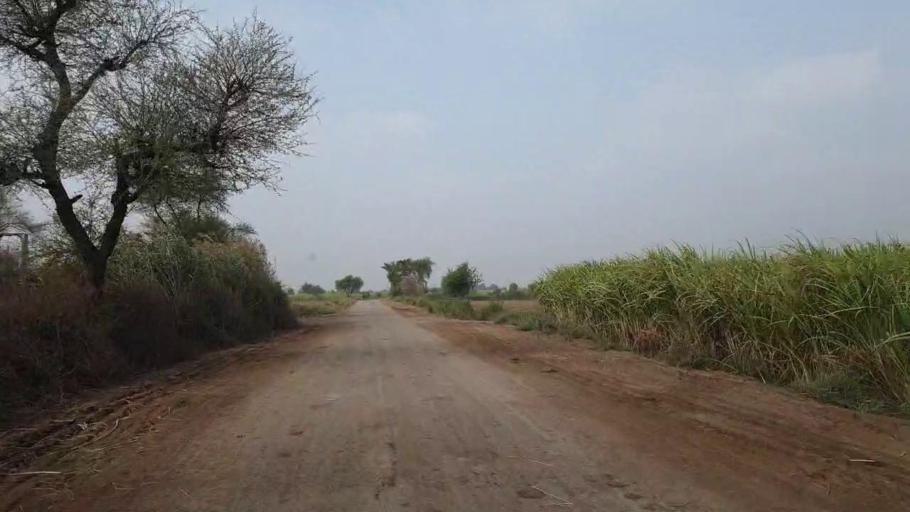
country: PK
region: Sindh
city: Tando Muhammad Khan
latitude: 25.1302
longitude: 68.5889
